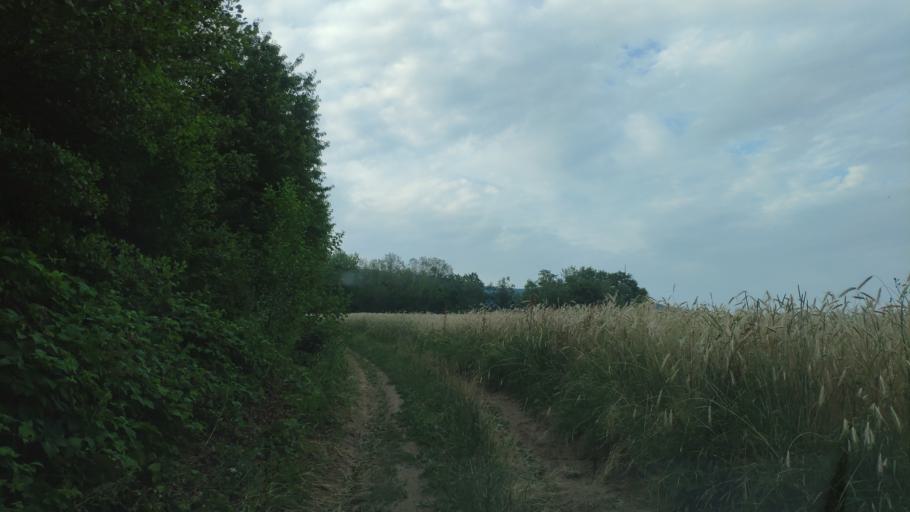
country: SK
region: Kosicky
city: Moldava nad Bodvou
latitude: 48.7080
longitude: 20.9915
